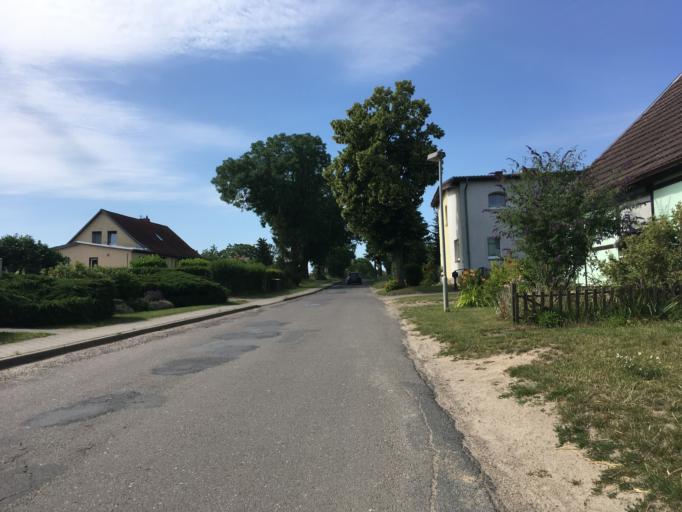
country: DE
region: Brandenburg
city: Gramzow
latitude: 53.2378
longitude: 14.0403
